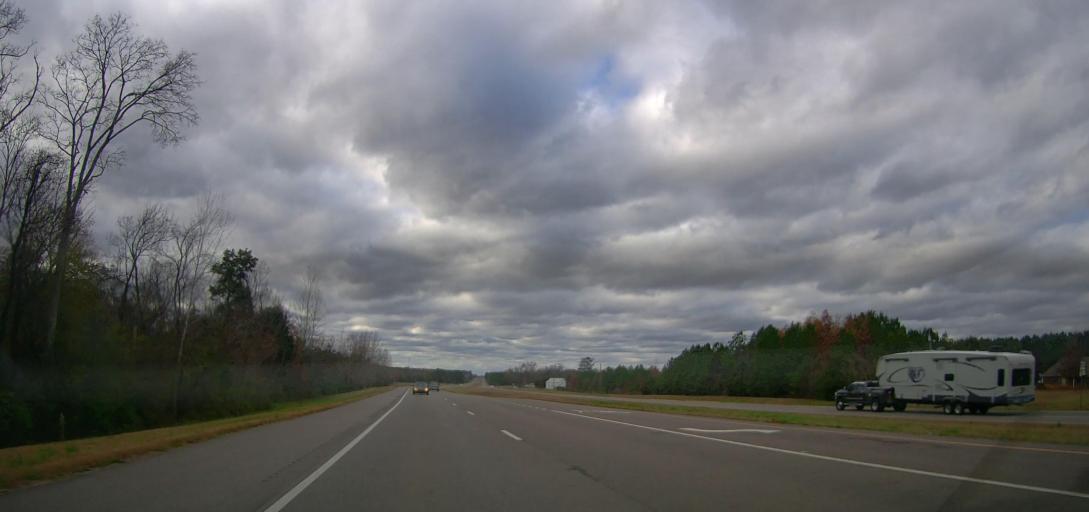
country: US
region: Alabama
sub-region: Morgan County
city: Danville
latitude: 34.3414
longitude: -87.0276
